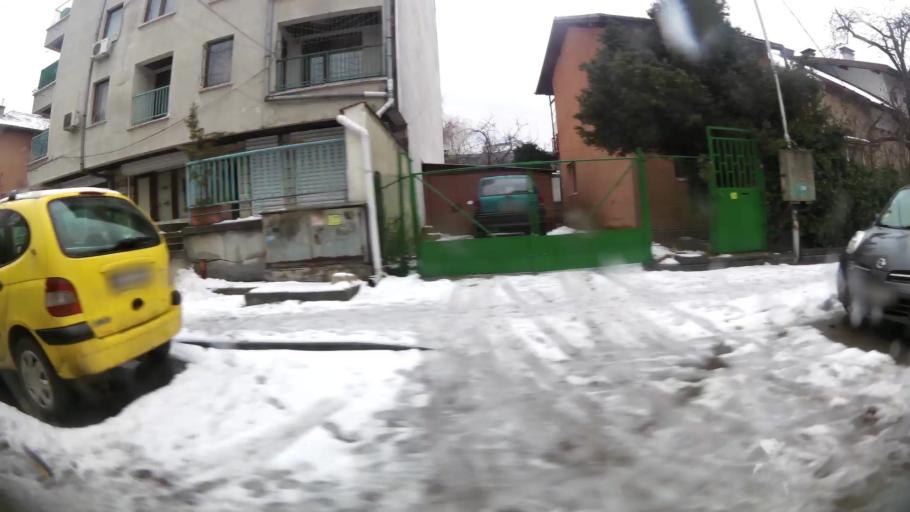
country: BG
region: Sofia-Capital
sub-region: Stolichna Obshtina
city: Sofia
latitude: 42.6656
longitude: 23.2681
